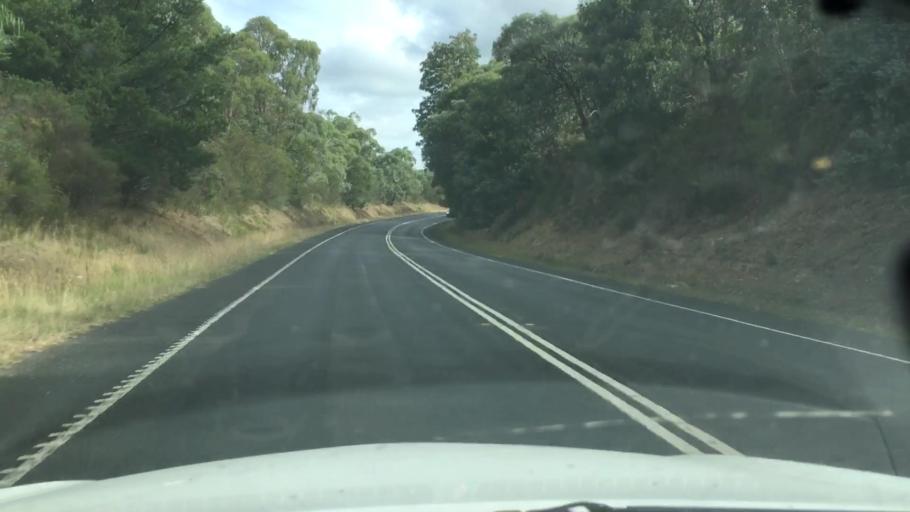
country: AU
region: Victoria
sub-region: Yarra Ranges
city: Selby
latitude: -37.9422
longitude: 145.3826
